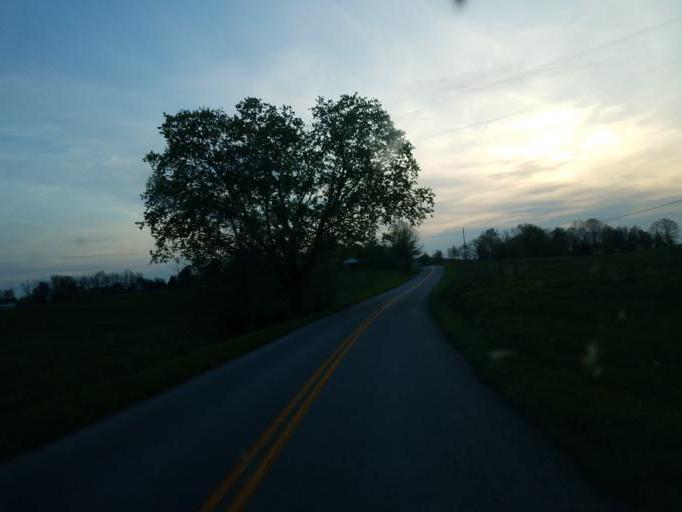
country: US
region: Kentucky
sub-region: Hart County
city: Munfordville
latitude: 37.2414
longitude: -85.7362
